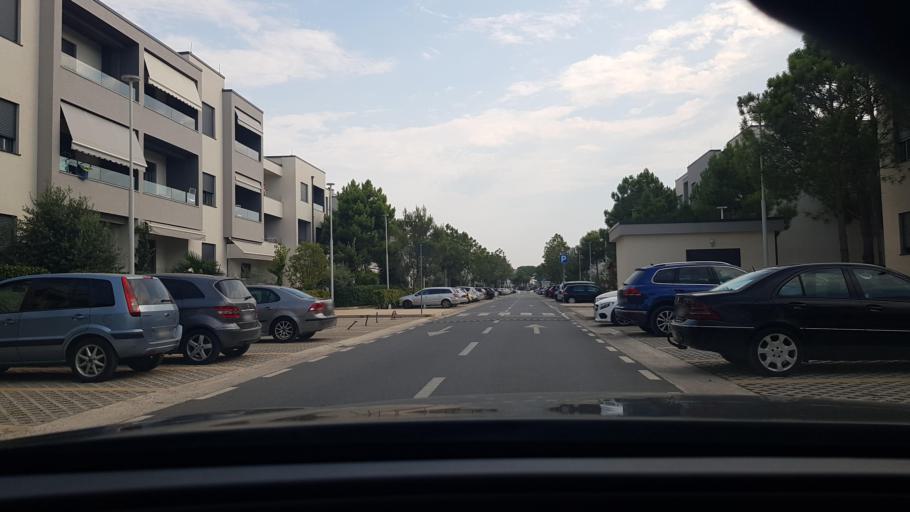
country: AL
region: Durres
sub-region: Rrethi i Durresit
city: Katundi i Ri
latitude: 41.4912
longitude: 19.5134
